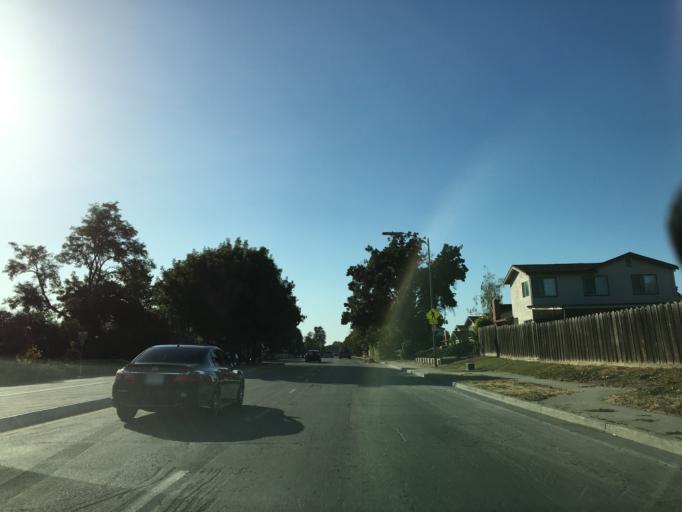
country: US
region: California
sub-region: Santa Clara County
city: San Jose
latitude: 37.3793
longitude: -121.8781
